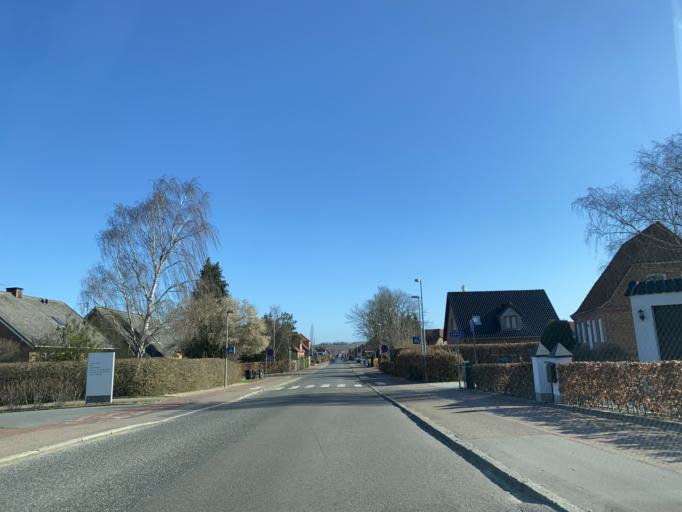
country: DK
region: Central Jutland
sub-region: Favrskov Kommune
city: Ulstrup
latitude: 56.3874
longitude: 9.7890
